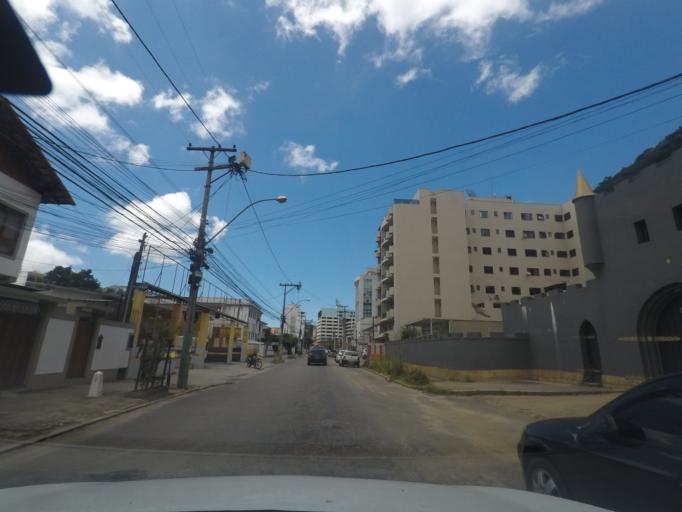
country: BR
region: Rio de Janeiro
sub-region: Teresopolis
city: Teresopolis
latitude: -22.4073
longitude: -42.9674
